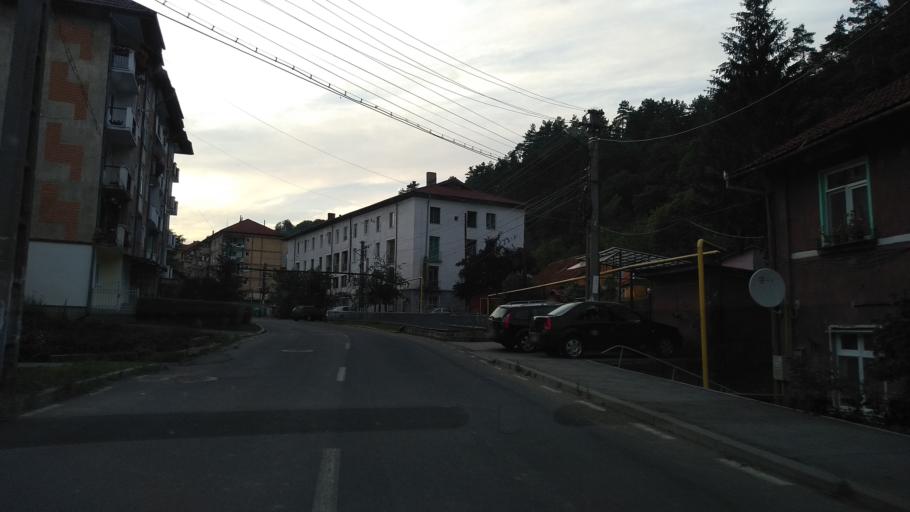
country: RO
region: Hunedoara
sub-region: Comuna Aninoasa
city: Aninoasa
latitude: 45.4062
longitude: 23.3193
